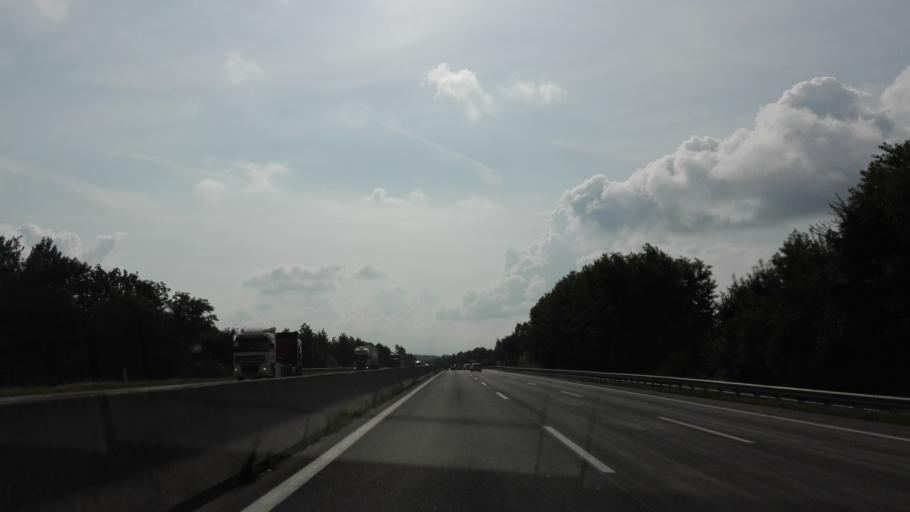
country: AT
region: Lower Austria
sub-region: Politischer Bezirk Amstetten
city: Zeillern
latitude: 48.1202
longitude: 14.7678
